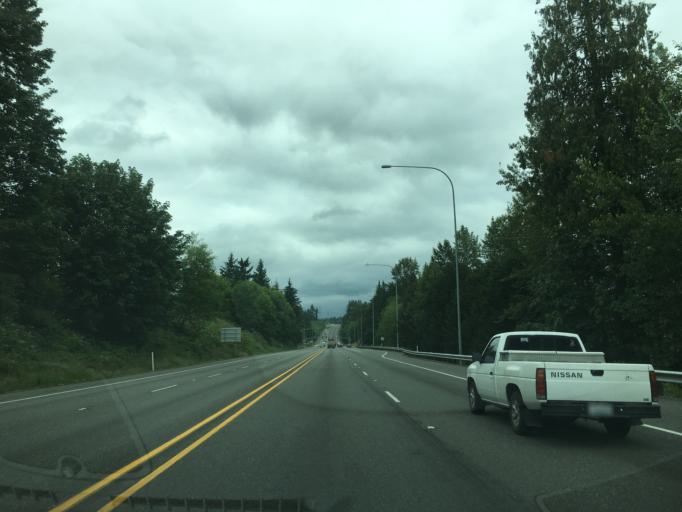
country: US
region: Washington
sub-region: Snohomish County
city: West Lake Stevens
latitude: 48.0095
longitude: -122.1074
